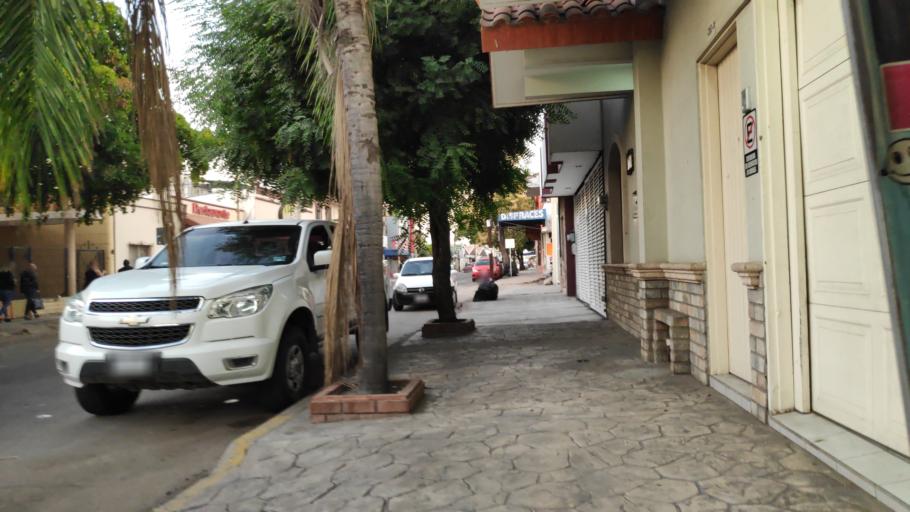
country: MX
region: Sinaloa
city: Culiacan
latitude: 24.8021
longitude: -107.3956
